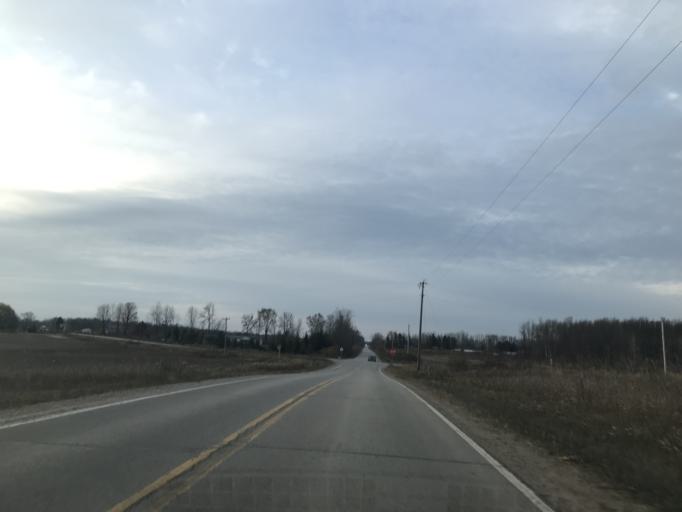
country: US
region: Wisconsin
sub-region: Marinette County
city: Peshtigo
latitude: 45.0946
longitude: -87.7994
